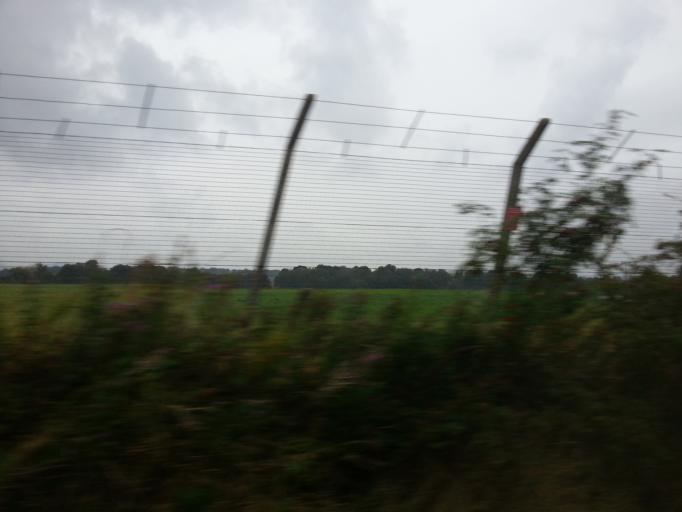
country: GB
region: Scotland
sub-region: Edinburgh
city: Currie
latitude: 55.9443
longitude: -3.3304
